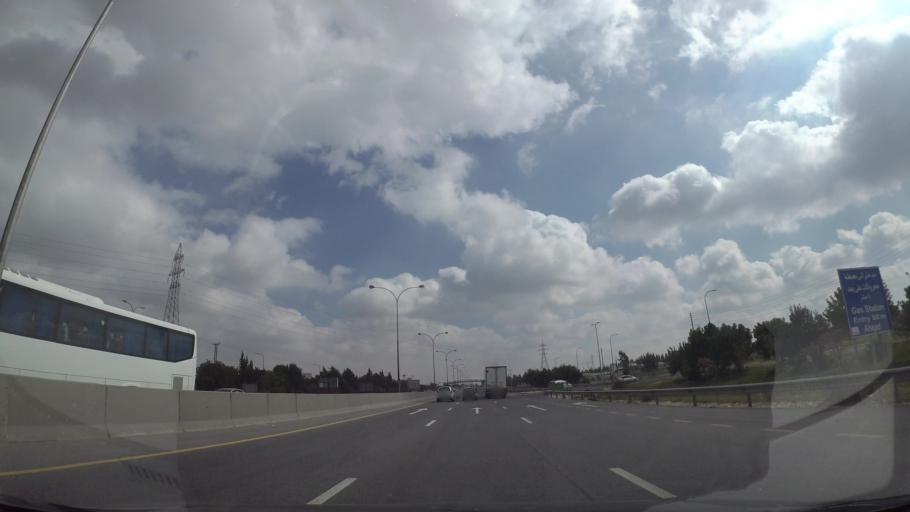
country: JO
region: Amman
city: Jawa
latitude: 31.8079
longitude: 35.9118
